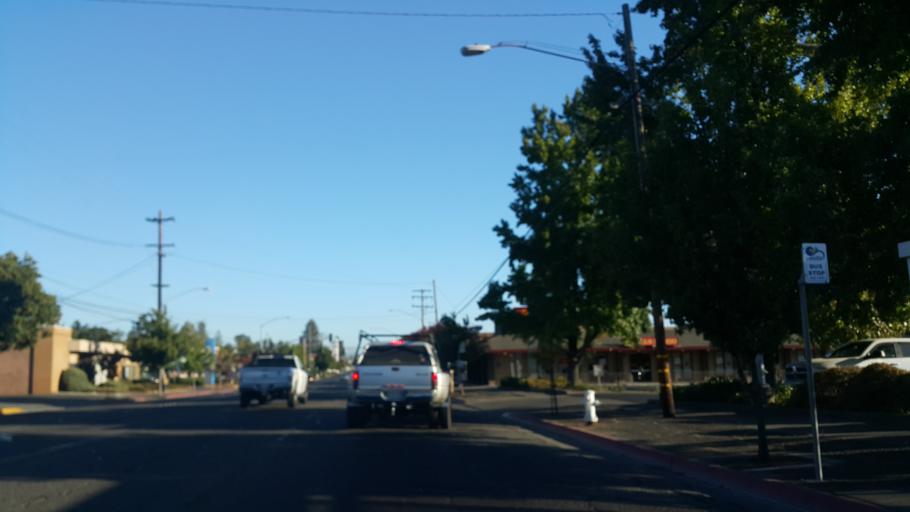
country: US
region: California
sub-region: Mendocino County
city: Ukiah
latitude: 39.1421
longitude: -123.2063
